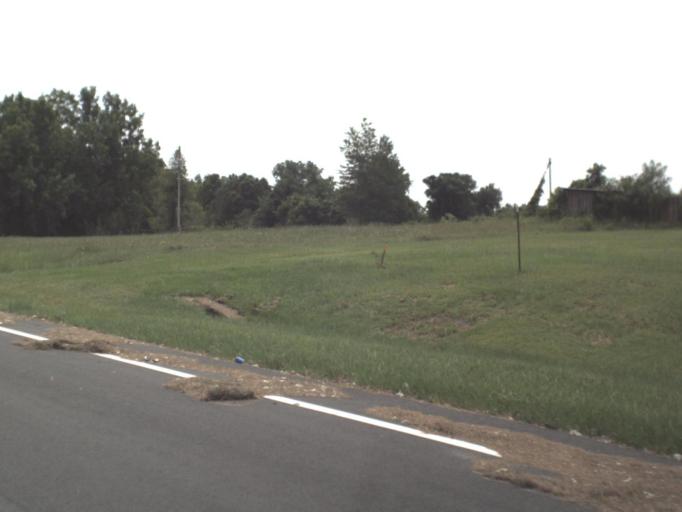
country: US
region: Florida
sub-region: Jefferson County
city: Monticello
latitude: 30.4720
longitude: -83.6545
